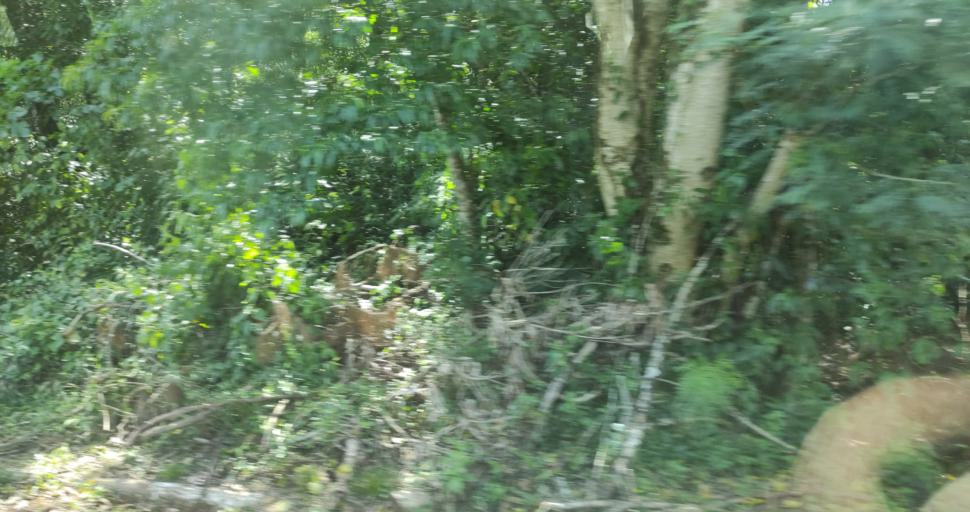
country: AR
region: Misiones
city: El Soberbio
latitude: -27.2847
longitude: -54.1981
